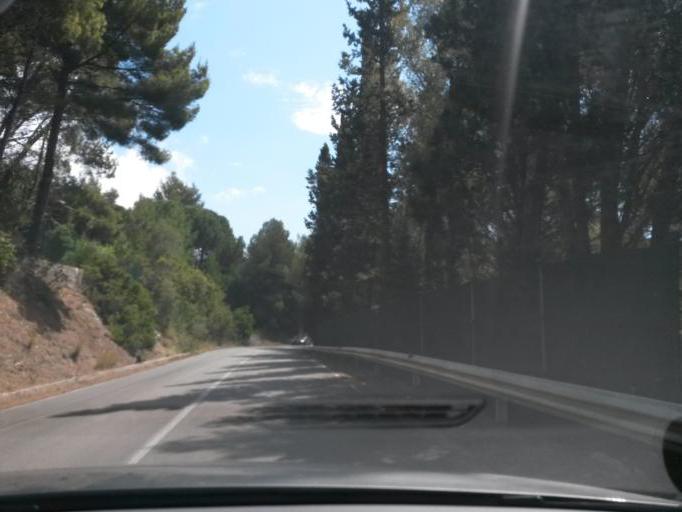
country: IT
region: Tuscany
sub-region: Provincia di Livorno
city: Marina di Campo
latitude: 42.7378
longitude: 10.2039
